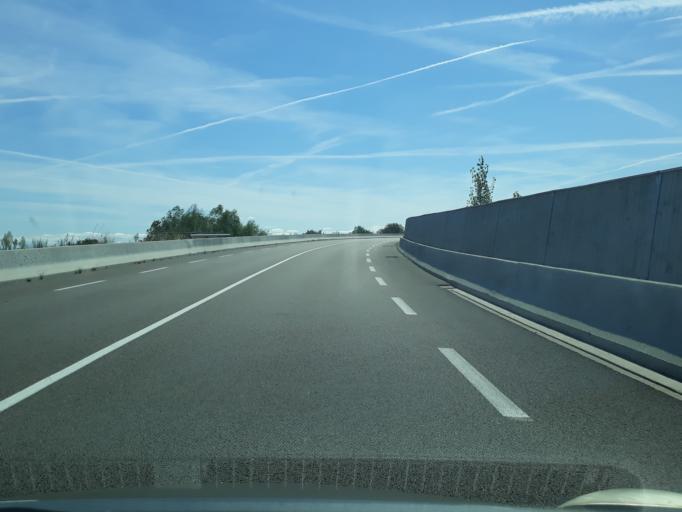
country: FR
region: Rhone-Alpes
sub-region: Departement de l'Ardeche
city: Davezieux
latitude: 45.2611
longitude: 4.7164
